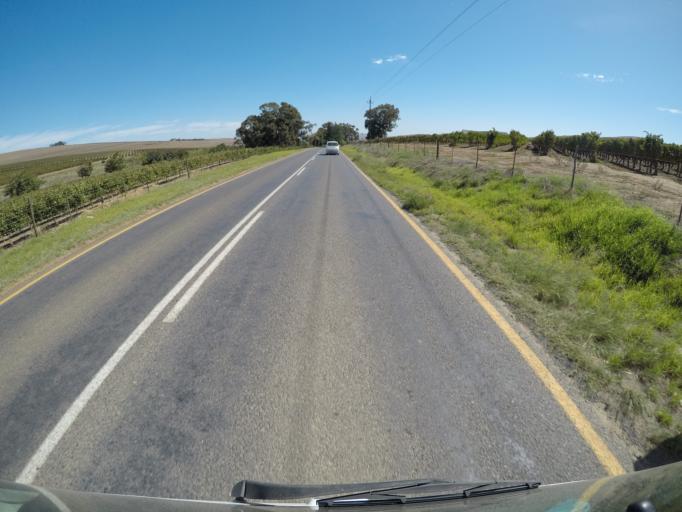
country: ZA
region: Western Cape
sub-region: City of Cape Town
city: Sunset Beach
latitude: -33.7888
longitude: 18.5943
